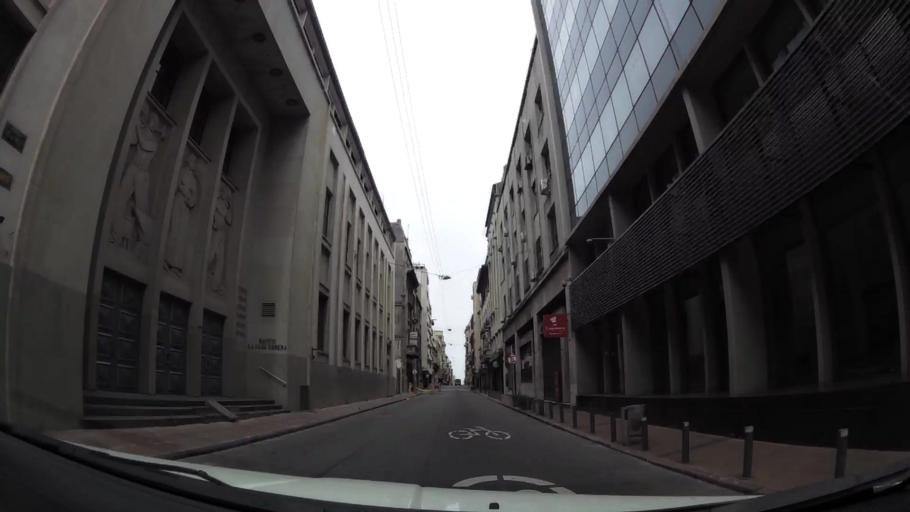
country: UY
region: Montevideo
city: Montevideo
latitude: -34.9059
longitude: -56.2059
